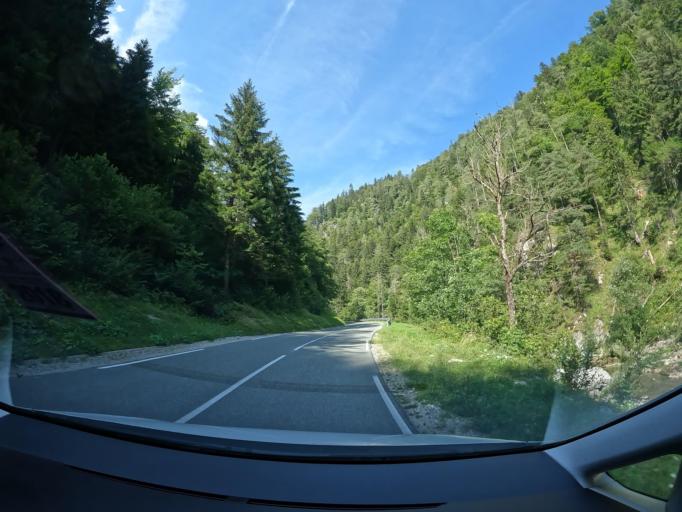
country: SI
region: Trzic
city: Bistrica pri Trzicu
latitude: 46.4305
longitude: 14.2400
